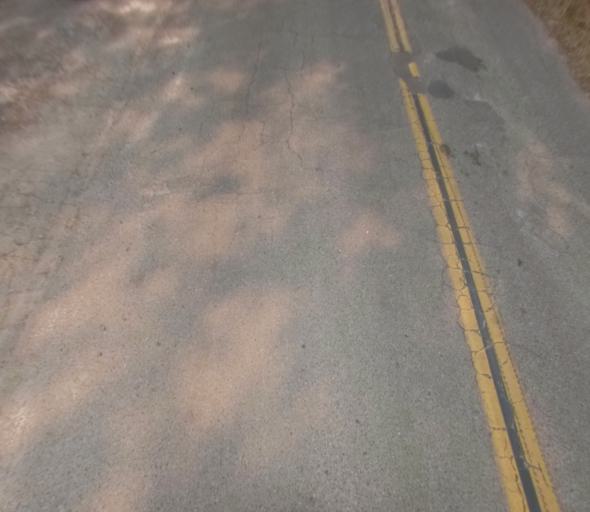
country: US
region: California
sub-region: Madera County
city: Oakhurst
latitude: 37.3052
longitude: -119.6166
